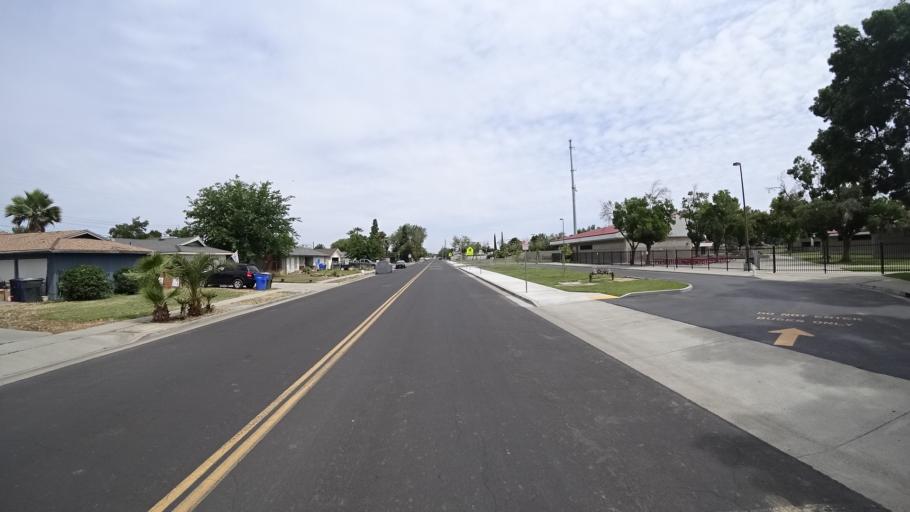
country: US
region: California
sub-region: Kings County
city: Hanford
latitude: 36.3520
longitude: -119.6397
